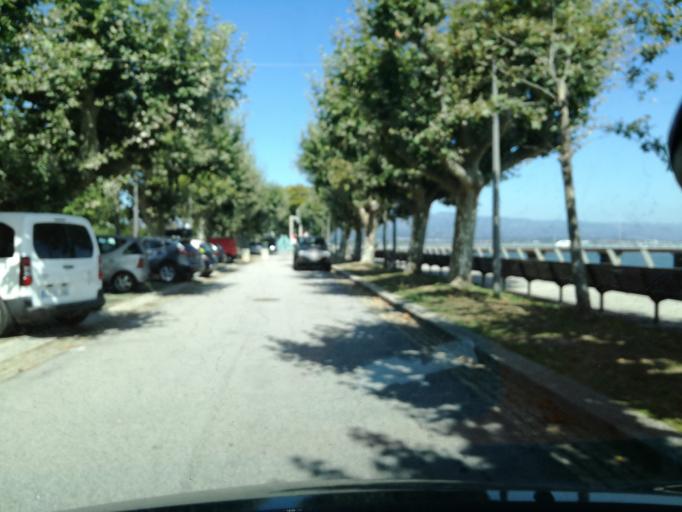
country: ES
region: Galicia
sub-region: Provincia de Pontevedra
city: A Guarda
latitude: 41.8771
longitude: -8.8346
